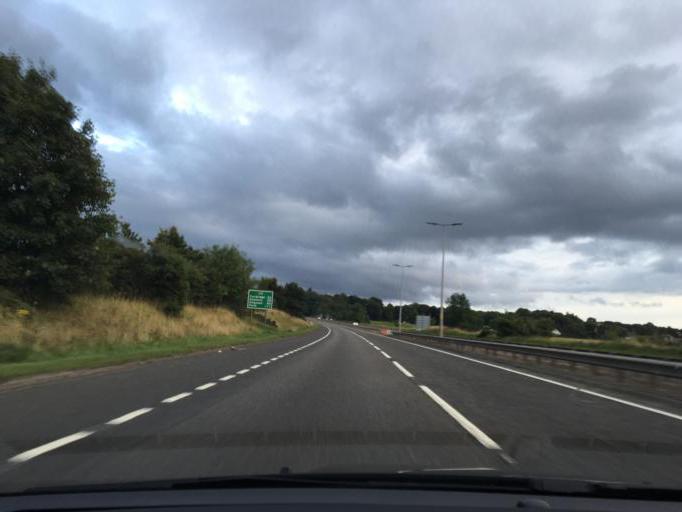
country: GB
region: Scotland
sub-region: Highland
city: Inverness
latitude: 57.4705
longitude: -4.1831
